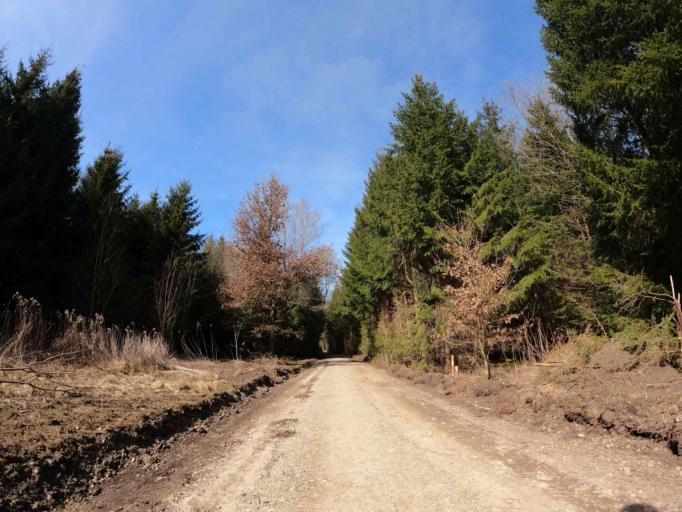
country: DE
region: Bavaria
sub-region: Upper Bavaria
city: Brunnthal
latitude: 47.9951
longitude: 11.7004
